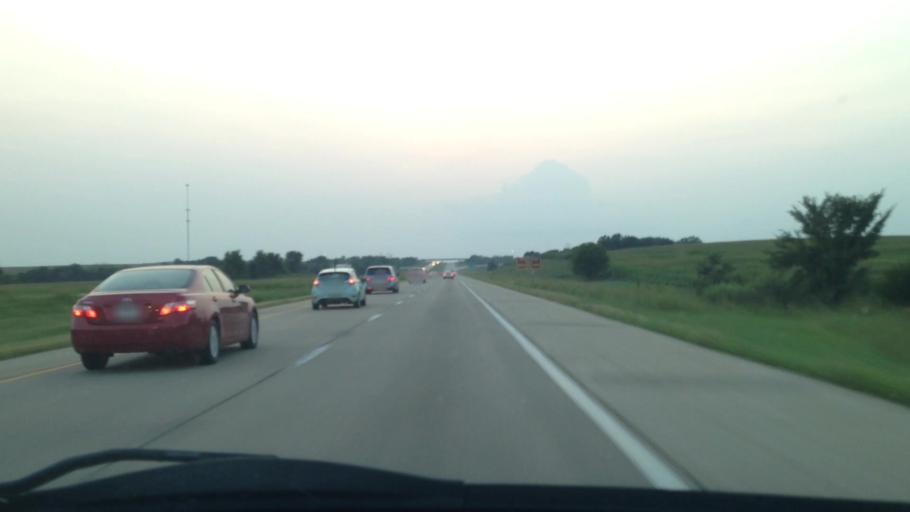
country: US
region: Iowa
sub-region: Buchanan County
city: Jesup
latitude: 42.3479
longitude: -92.0478
